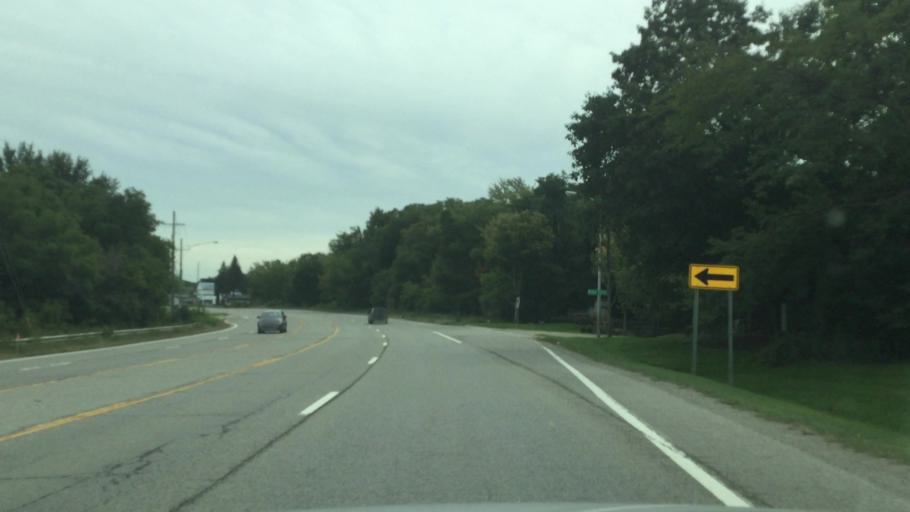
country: US
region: Michigan
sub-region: Oakland County
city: Clarkston
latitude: 42.7521
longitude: -83.4786
